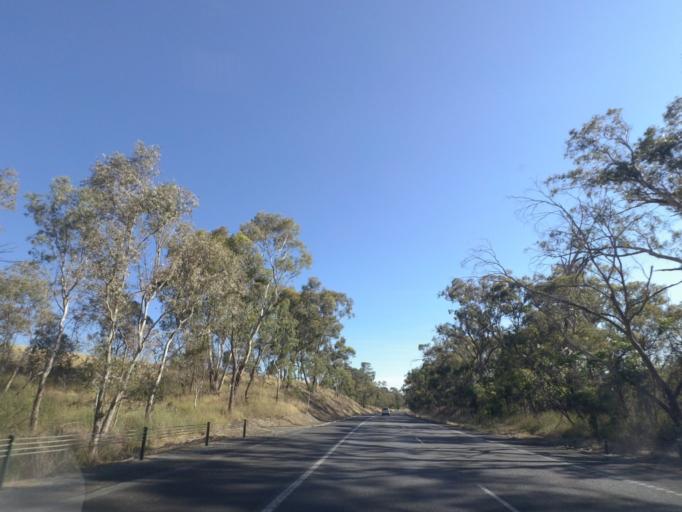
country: AU
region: Victoria
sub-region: Murrindindi
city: Kinglake West
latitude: -37.1686
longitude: 145.0773
